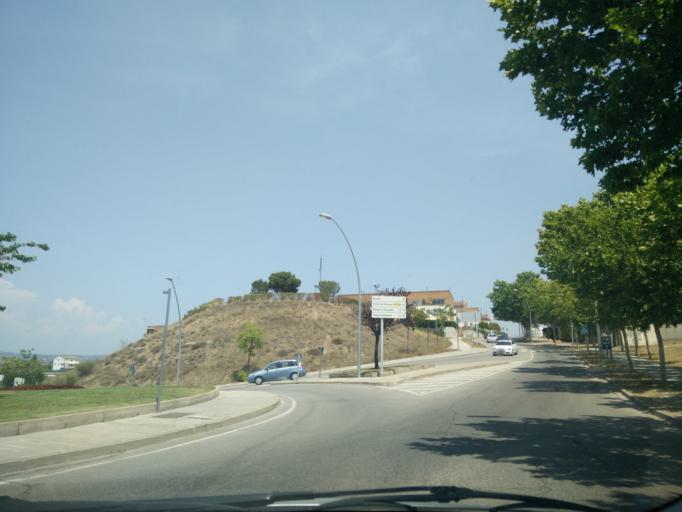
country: ES
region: Catalonia
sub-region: Provincia de Barcelona
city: Manresa
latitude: 41.7208
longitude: 1.8407
